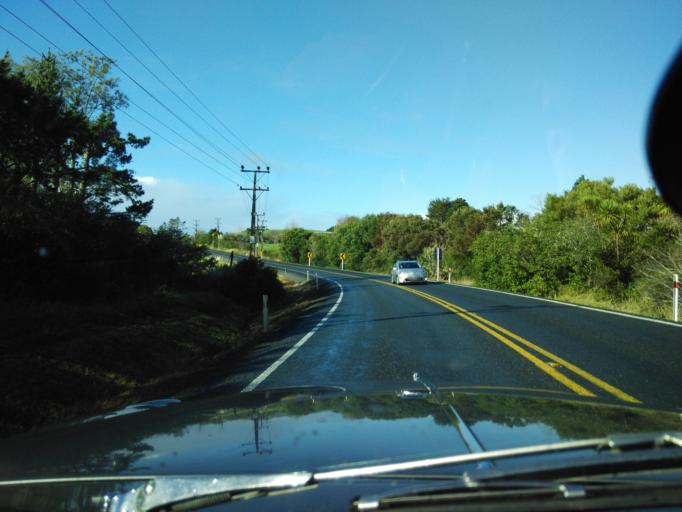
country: NZ
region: Auckland
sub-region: Auckland
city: Parakai
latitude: -36.6353
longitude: 174.5279
